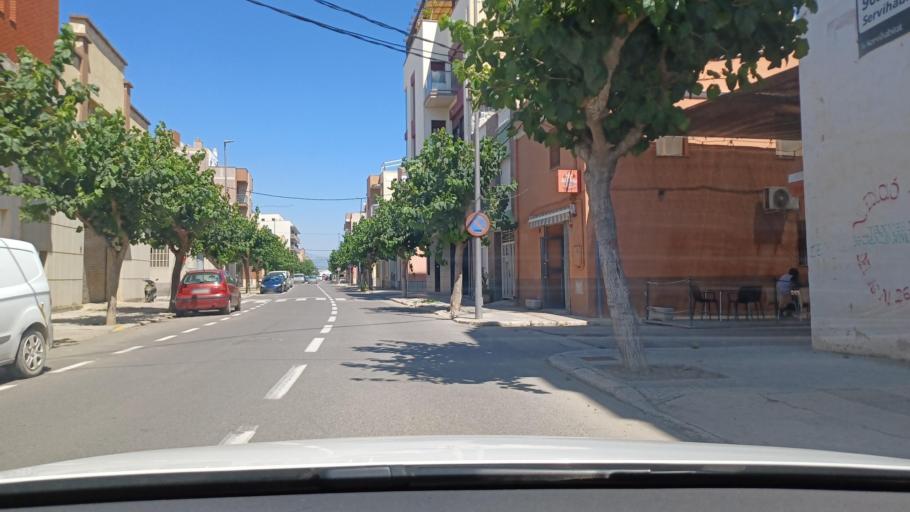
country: ES
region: Catalonia
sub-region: Provincia de Tarragona
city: Amposta
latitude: 40.7107
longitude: 0.5859
